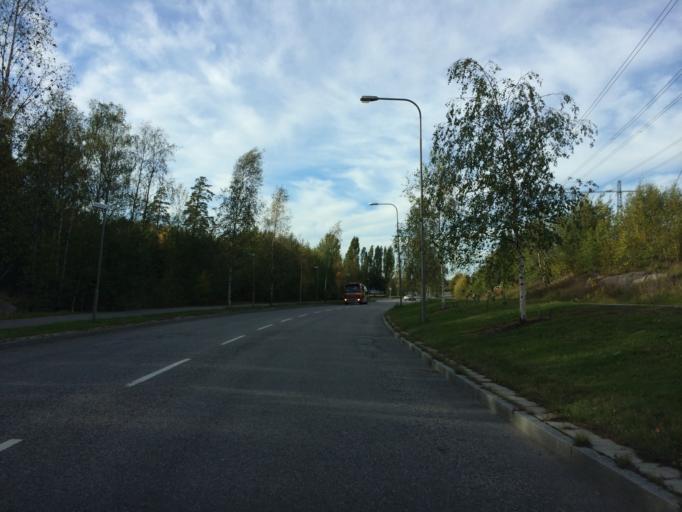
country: SE
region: Stockholm
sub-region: Stockholms Kommun
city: Kista
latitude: 59.4207
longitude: 17.9215
